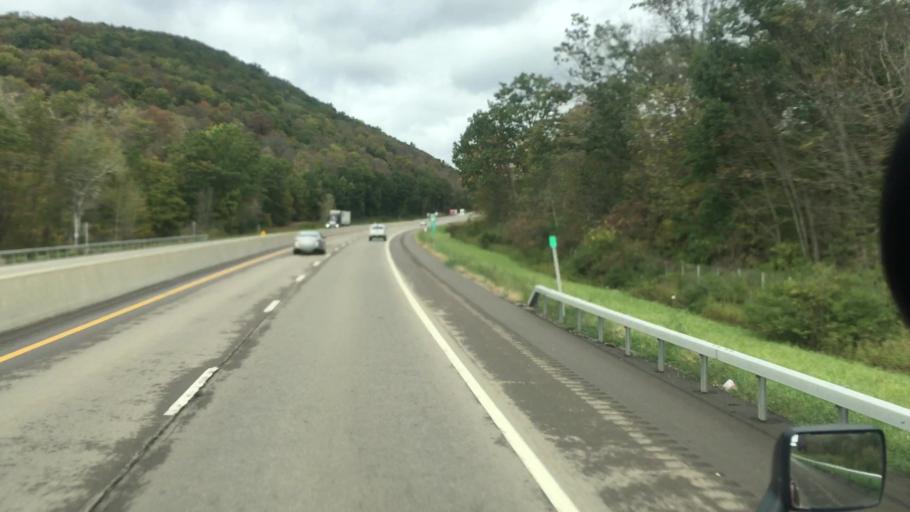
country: US
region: New York
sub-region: Cattaraugus County
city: Salamanca
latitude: 42.1048
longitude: -78.6624
